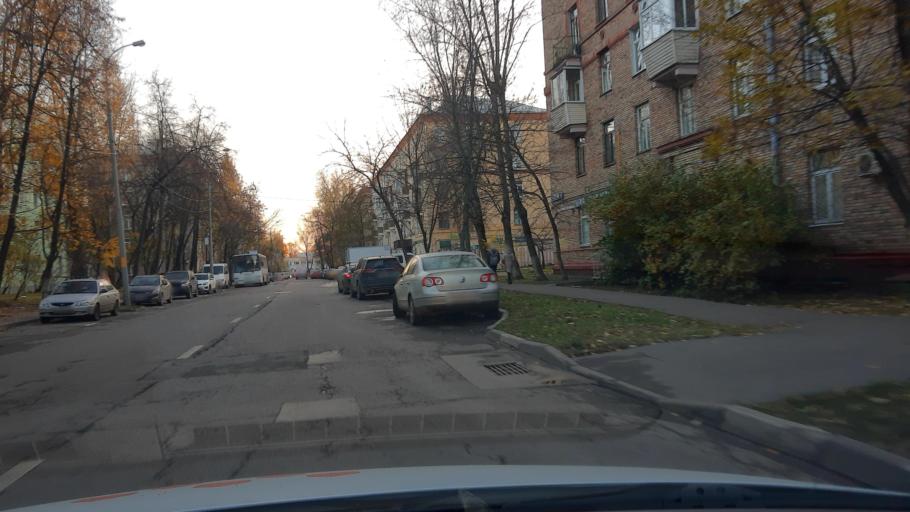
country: RU
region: Moscow
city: Novyye Kuz'minki
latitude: 55.6961
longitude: 37.7479
